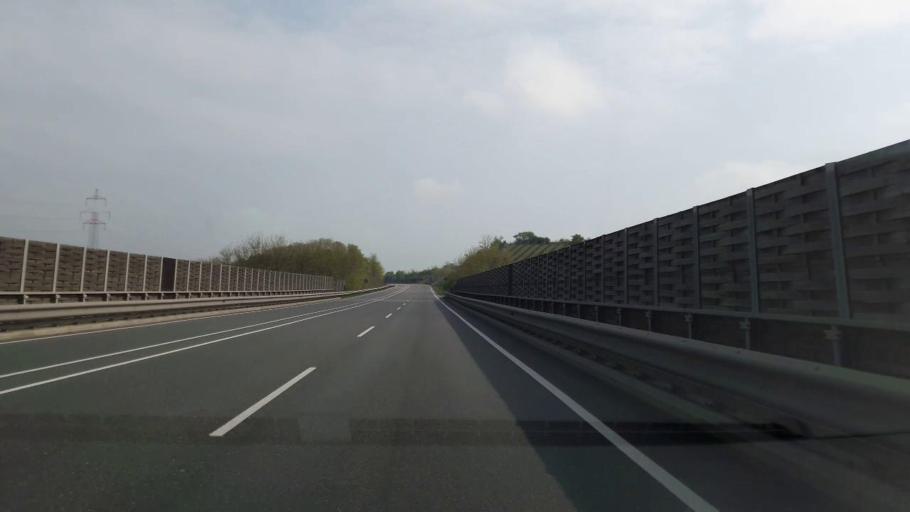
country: AT
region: Lower Austria
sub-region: Politischer Bezirk Hollabrunn
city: Haugsdorf
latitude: 48.7306
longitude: 16.0535
